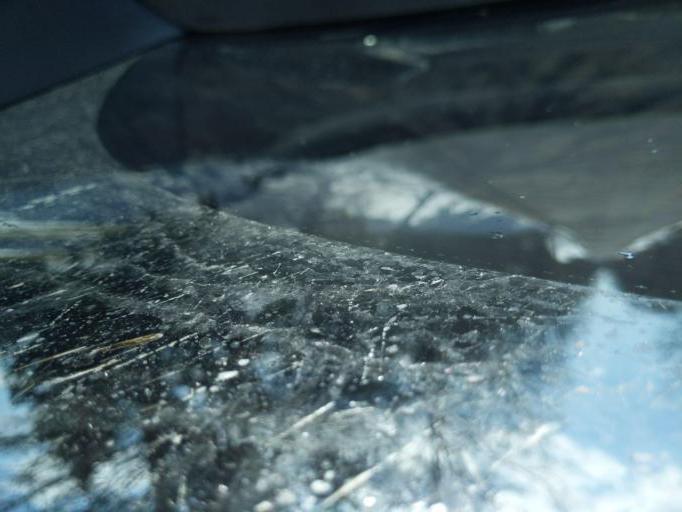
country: US
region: Michigan
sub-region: Livingston County
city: Fowlerville
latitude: 42.5822
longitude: -84.0890
